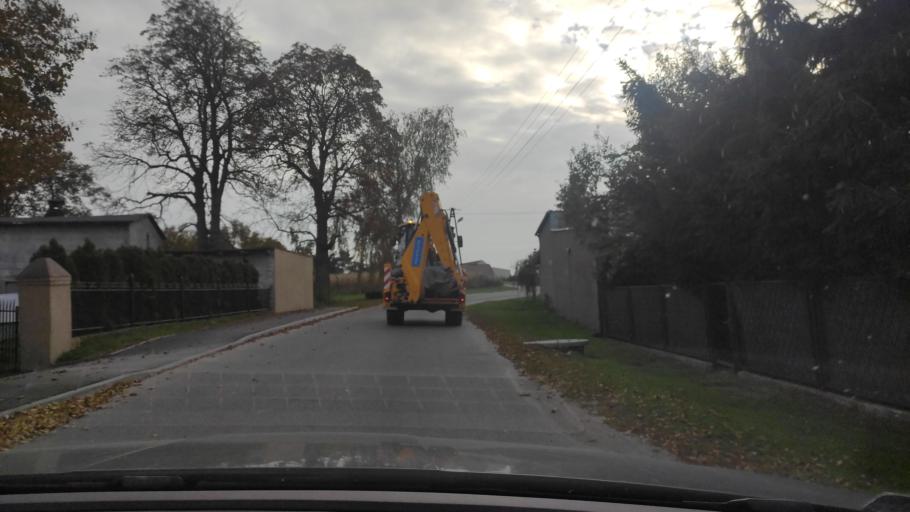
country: PL
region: Greater Poland Voivodeship
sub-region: Powiat poznanski
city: Kostrzyn
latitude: 52.4463
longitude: 17.2114
